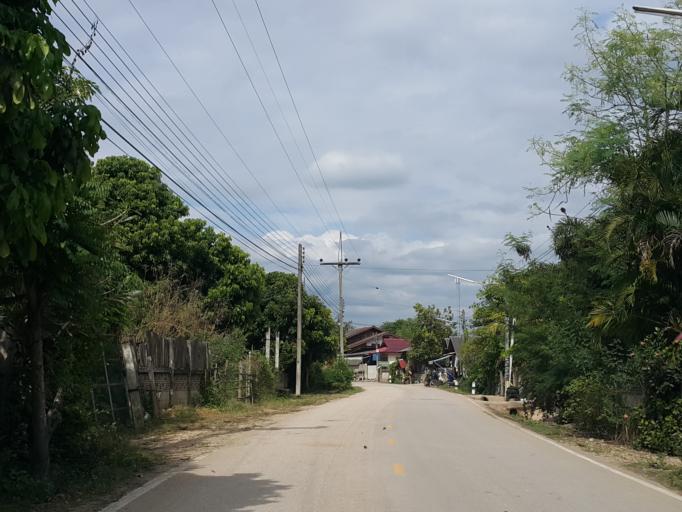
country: TH
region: Lampang
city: Chae Hom
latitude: 18.5629
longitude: 99.4589
